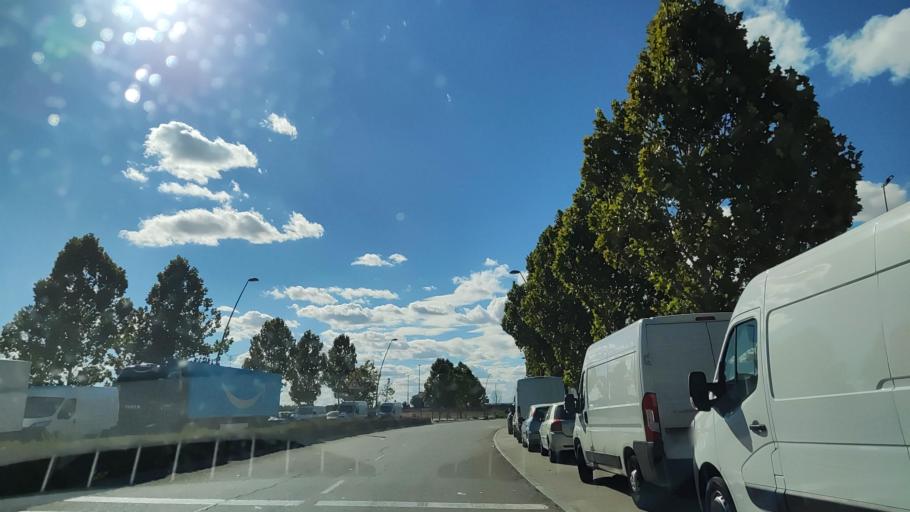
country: ES
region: Madrid
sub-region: Provincia de Madrid
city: Pinto
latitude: 40.2754
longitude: -3.6834
